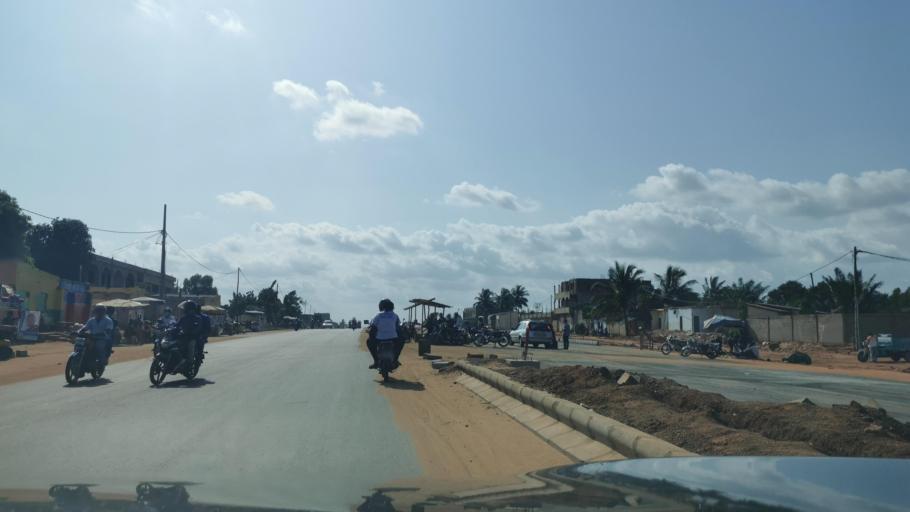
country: TG
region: Maritime
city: Lome
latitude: 6.2170
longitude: 1.1293
